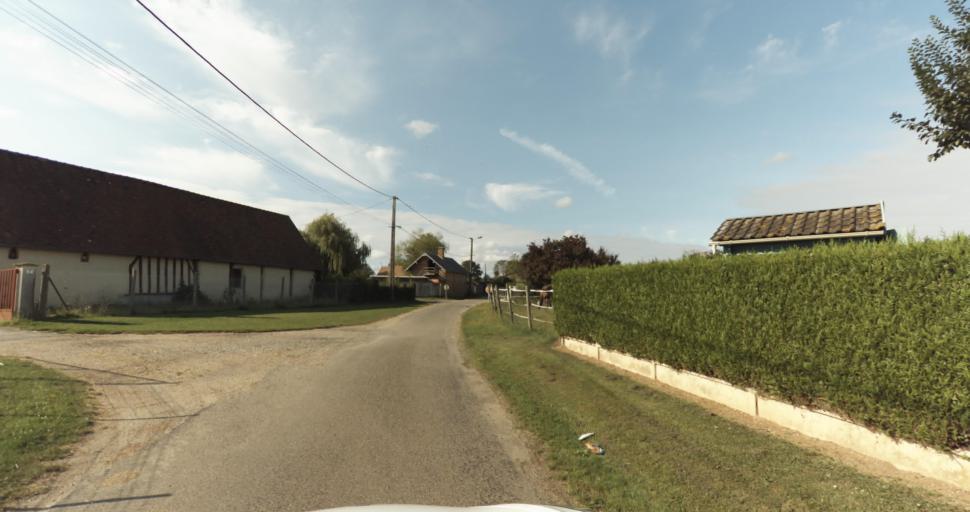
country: FR
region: Haute-Normandie
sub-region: Departement de l'Eure
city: Tillieres-sur-Avre
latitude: 48.7951
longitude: 1.0973
